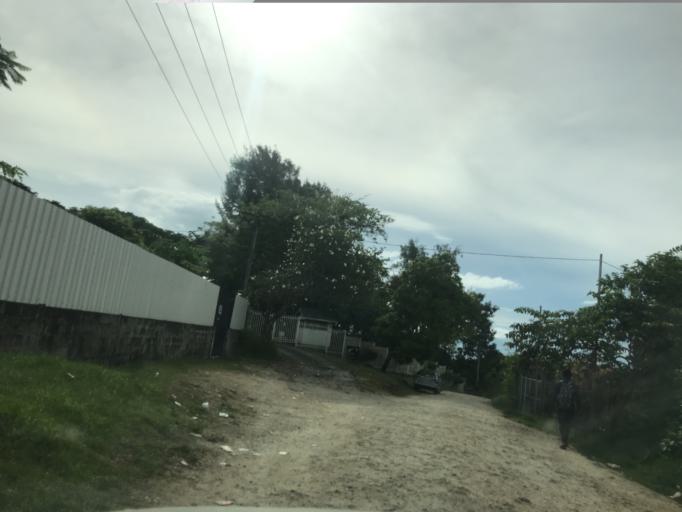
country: SB
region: Guadalcanal
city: Honiara
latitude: -9.4360
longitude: 159.9432
